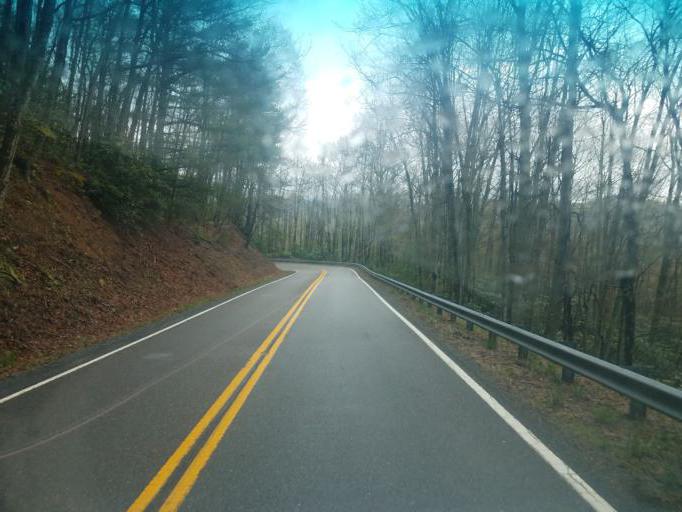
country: US
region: Virginia
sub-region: Smyth County
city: Chilhowie
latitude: 36.6552
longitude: -81.6816
